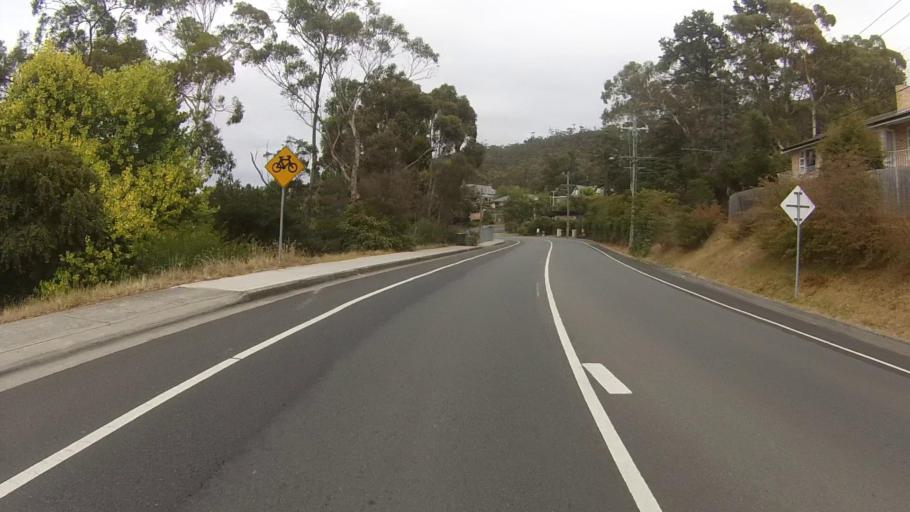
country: AU
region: Tasmania
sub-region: Kingborough
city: Taroona
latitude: -42.9342
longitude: 147.3554
